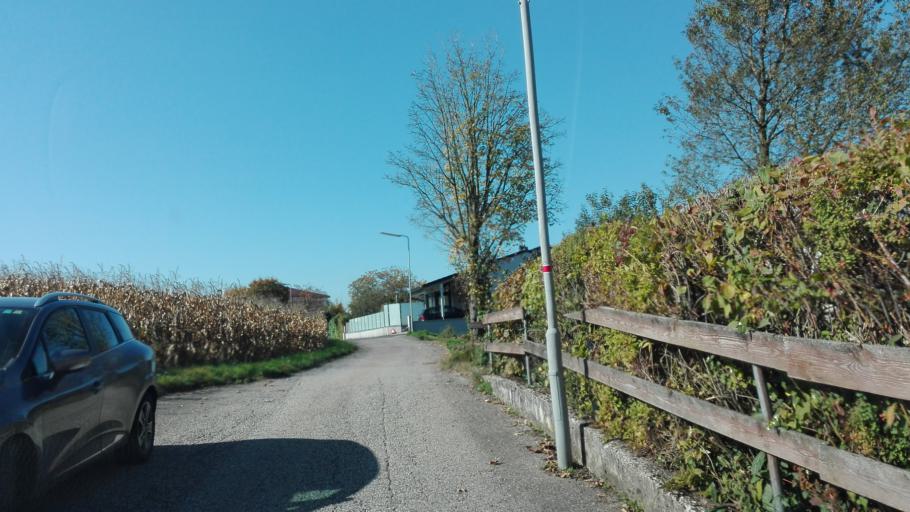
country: AT
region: Upper Austria
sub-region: Politischer Bezirk Linz-Land
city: Leonding
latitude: 48.2828
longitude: 14.2727
